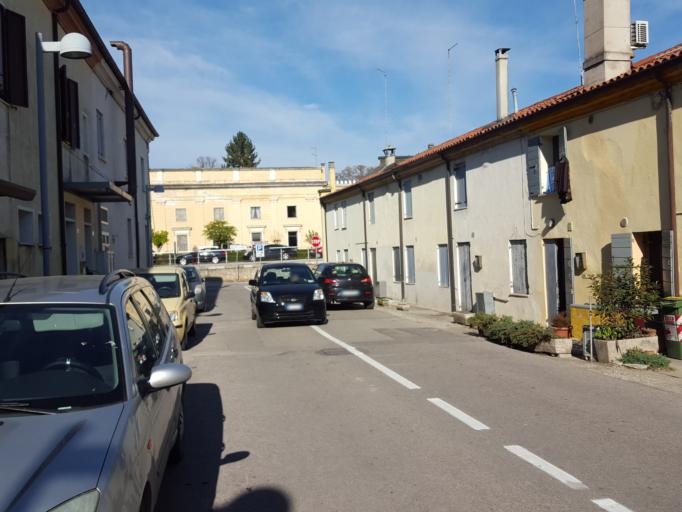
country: IT
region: Veneto
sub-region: Provincia di Padova
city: Piazzola sul Brenta
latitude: 45.5432
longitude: 11.7879
